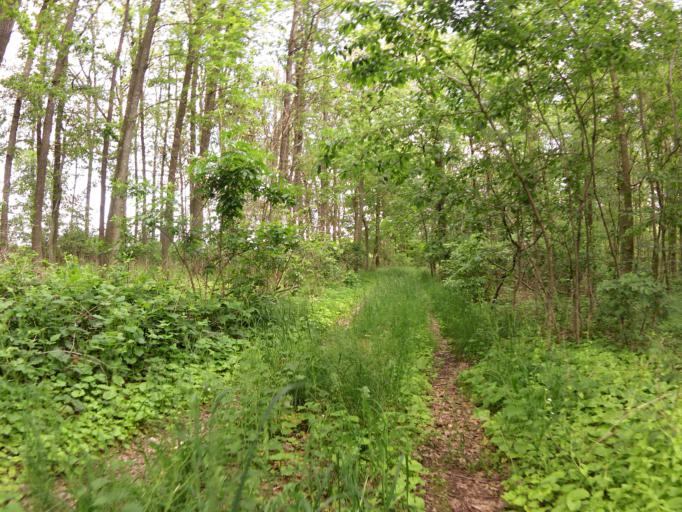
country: DE
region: Bavaria
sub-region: Regierungsbezirk Unterfranken
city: Theilheim
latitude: 49.7335
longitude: 10.0515
